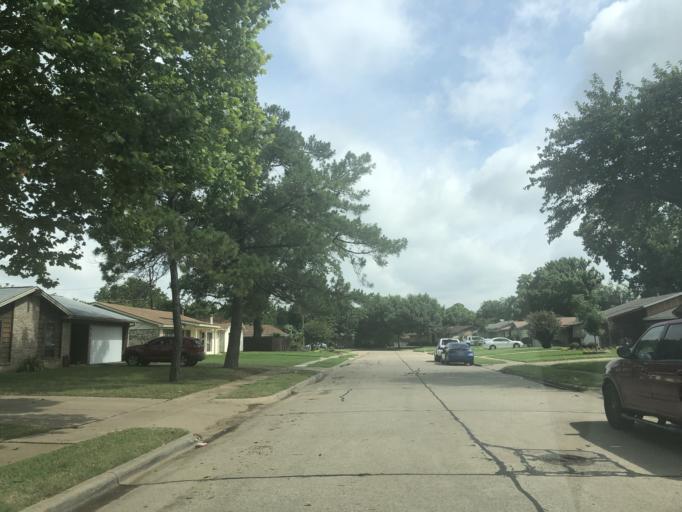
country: US
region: Texas
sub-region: Dallas County
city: Irving
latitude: 32.7936
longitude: -96.9746
